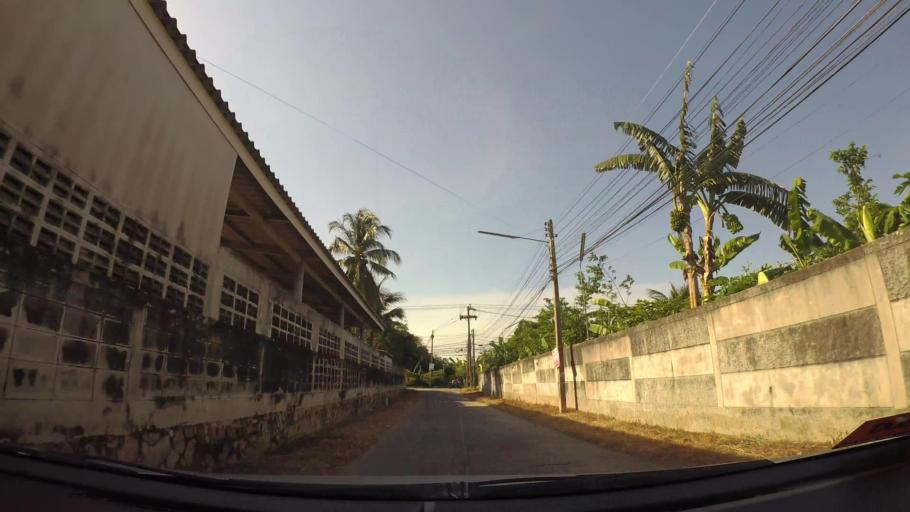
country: TH
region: Chon Buri
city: Si Racha
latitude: 13.1551
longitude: 100.9355
